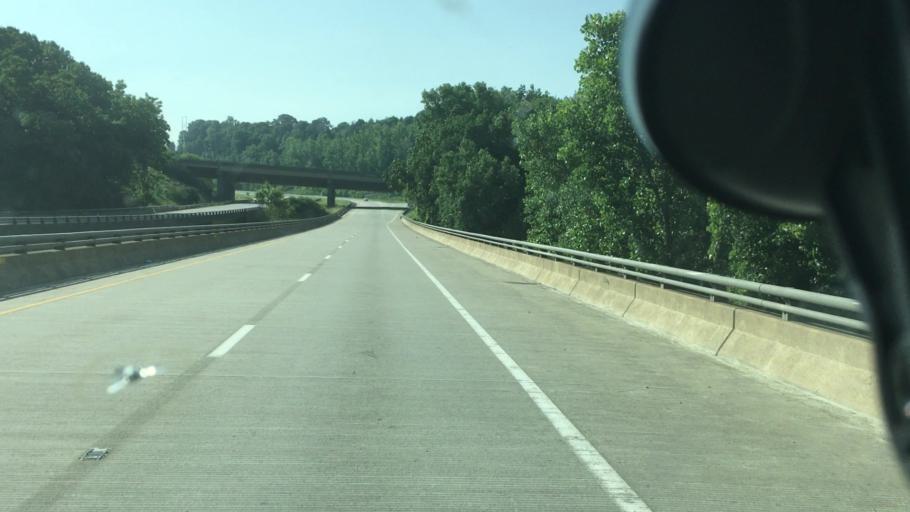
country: US
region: Pennsylvania
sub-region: Lawrence County
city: Oakland
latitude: 40.9713
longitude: -80.3675
